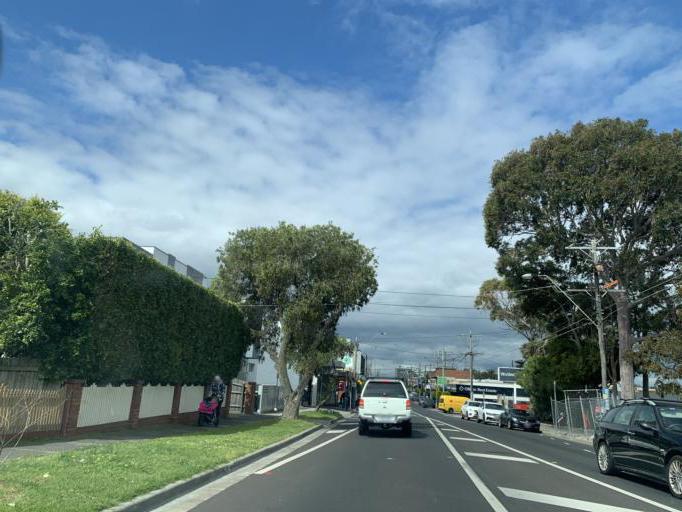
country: AU
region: Victoria
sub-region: Kingston
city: Mentone
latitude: -37.9809
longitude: 145.0622
